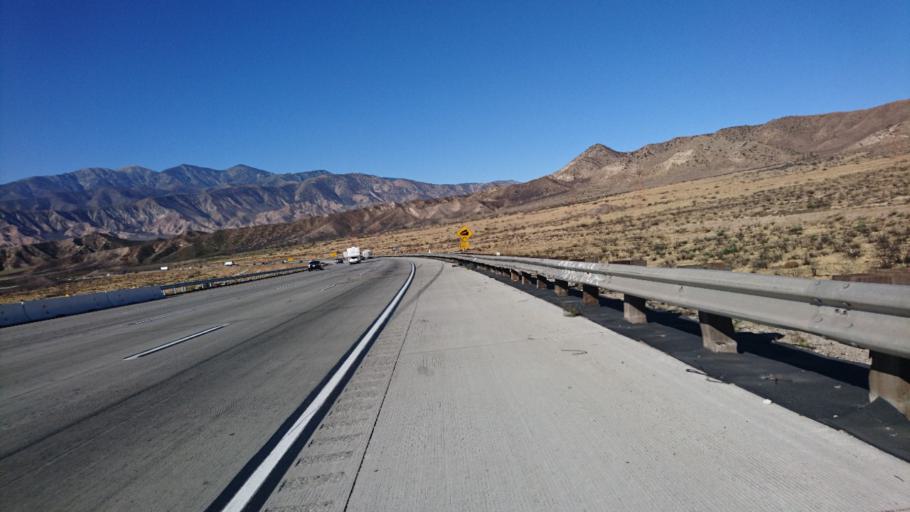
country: US
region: California
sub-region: San Bernardino County
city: Oak Hills
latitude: 34.3480
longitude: -117.4717
